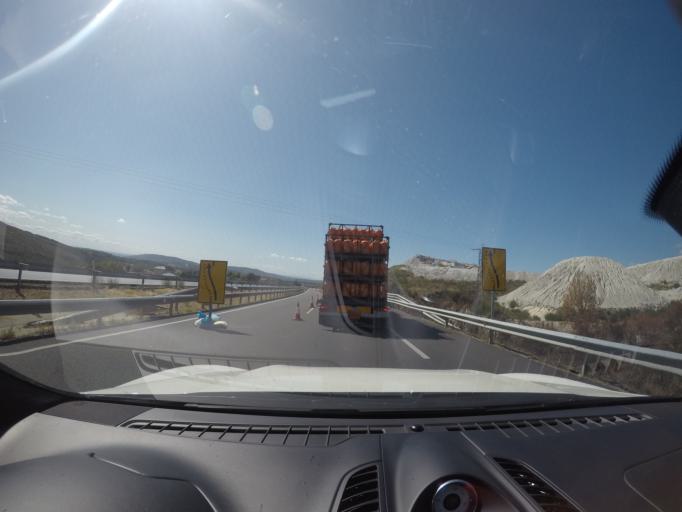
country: ES
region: Castille and Leon
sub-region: Provincia de Zamora
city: Pias
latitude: 42.0423
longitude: -7.0061
